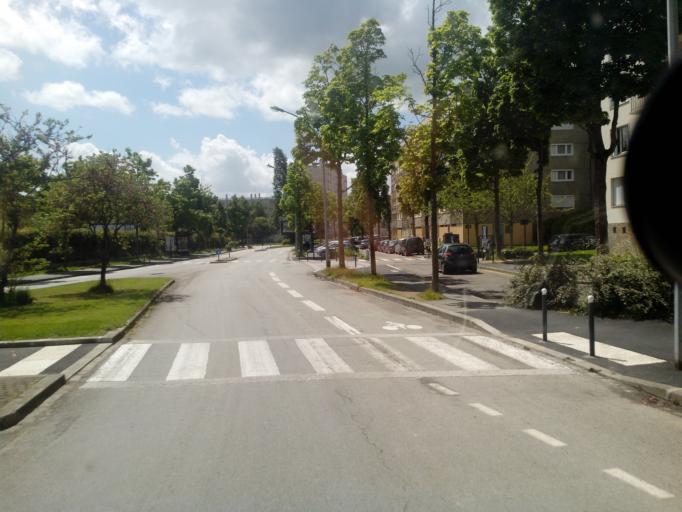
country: FR
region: Brittany
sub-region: Departement d'Ille-et-Vilaine
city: Rennes
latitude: 48.1175
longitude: -1.7047
